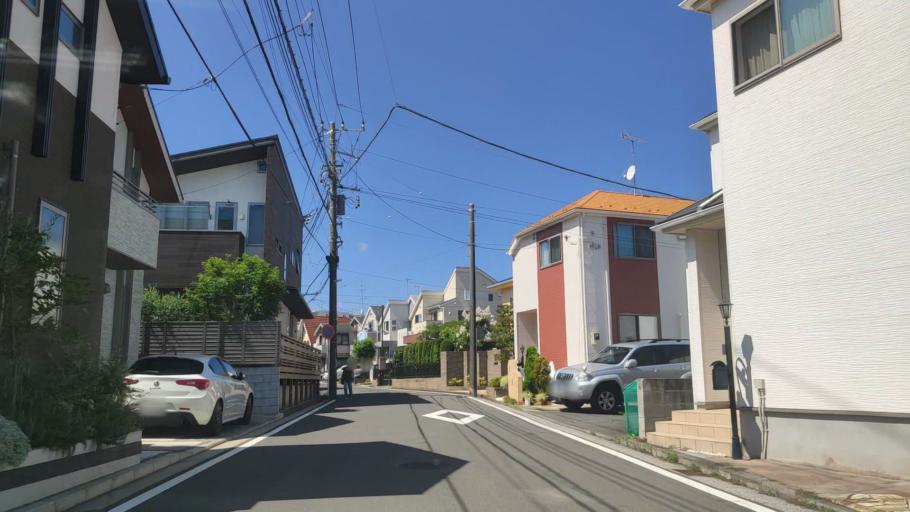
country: JP
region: Kanagawa
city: Yokohama
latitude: 35.5135
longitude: 139.6389
